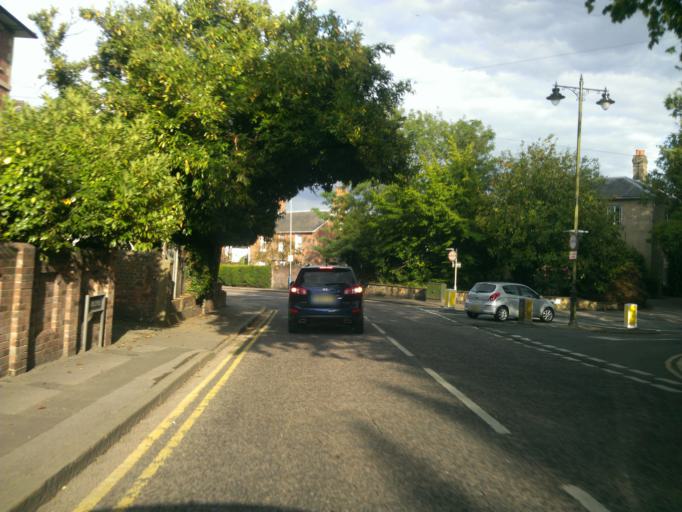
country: GB
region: England
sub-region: Kent
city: Tonbridge
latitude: 51.1978
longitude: 0.2787
